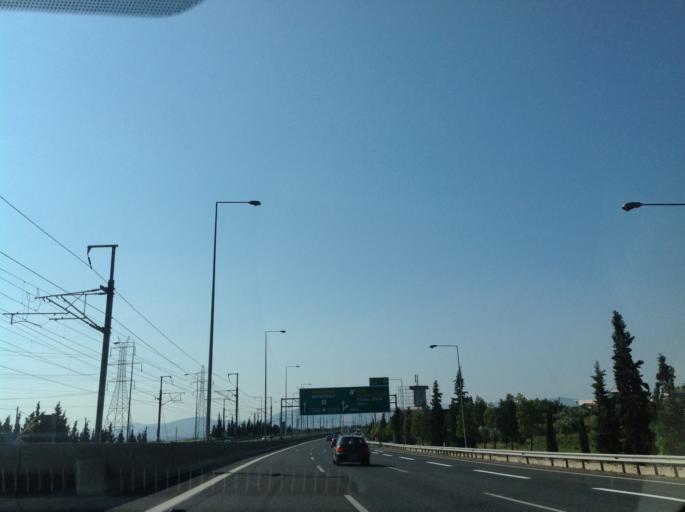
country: GR
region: Attica
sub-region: Nomarchia Anatolikis Attikis
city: Argithea
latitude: 37.9678
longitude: 23.8823
